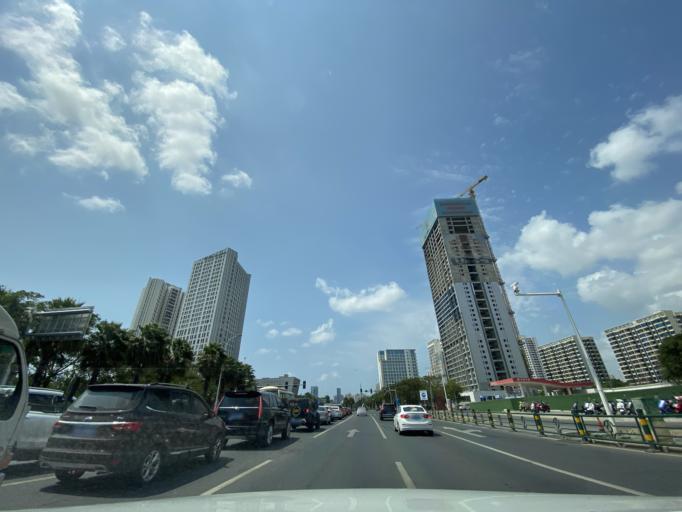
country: CN
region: Hainan
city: Sanya
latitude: 18.2907
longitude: 109.5254
